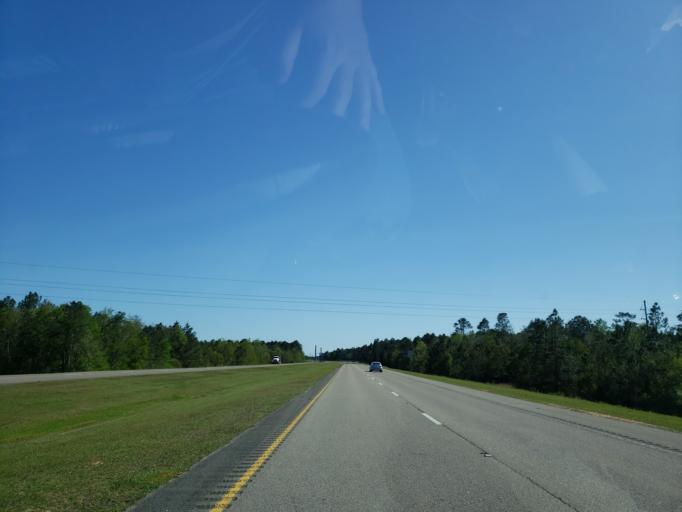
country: US
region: Mississippi
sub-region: Harrison County
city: Lyman
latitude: 30.4802
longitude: -89.0289
